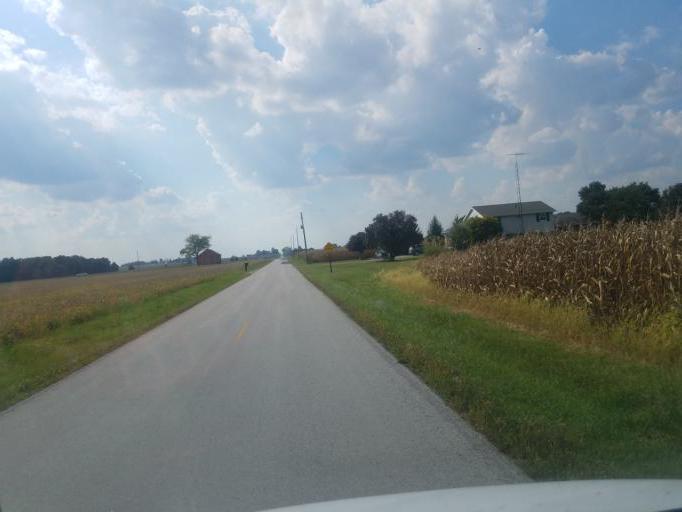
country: US
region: Ohio
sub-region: Hardin County
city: Kenton
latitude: 40.7463
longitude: -83.6282
